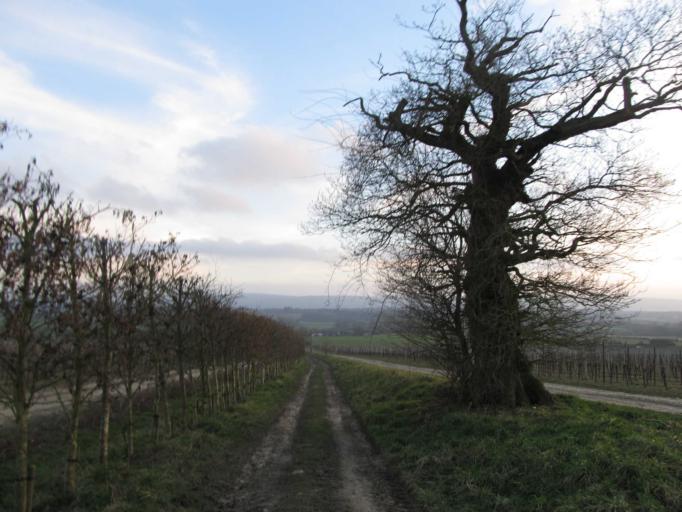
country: GB
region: England
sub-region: West Sussex
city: Petworth
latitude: 50.9922
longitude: -0.6580
